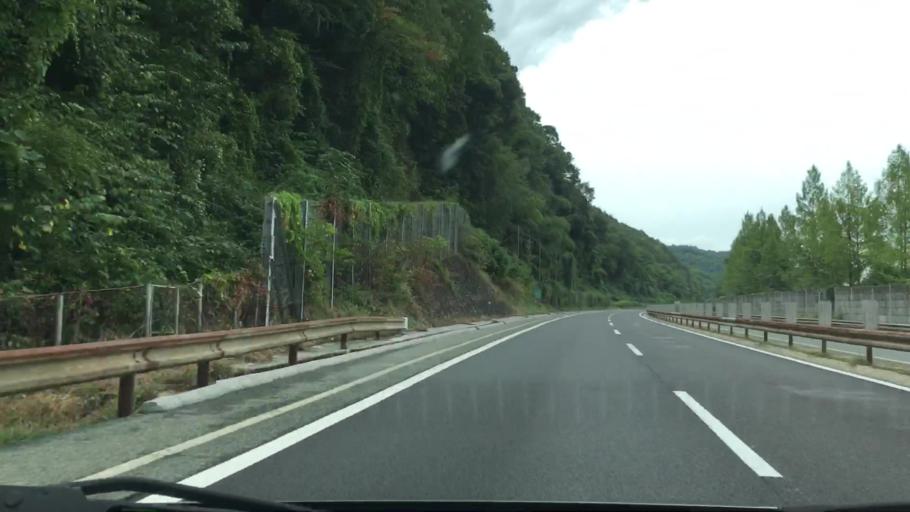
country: JP
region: Okayama
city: Niimi
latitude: 34.9724
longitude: 133.6236
